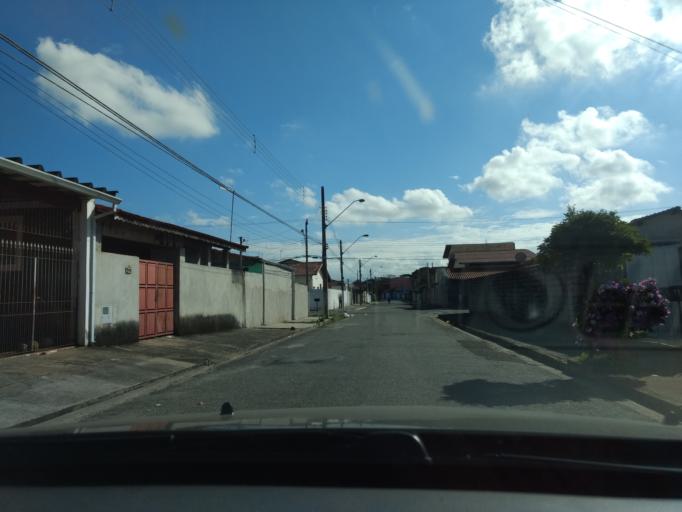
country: BR
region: Sao Paulo
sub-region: Tremembe
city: Tremembe
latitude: -22.9941
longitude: -45.5295
